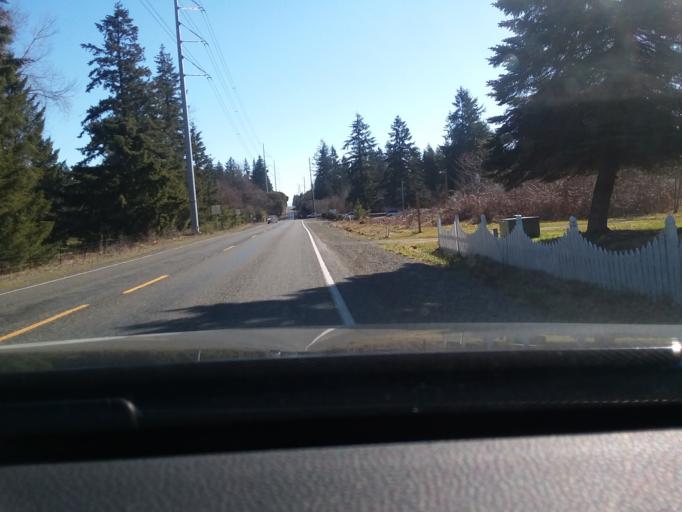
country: US
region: Washington
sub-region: Pierce County
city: Waller
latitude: 47.1807
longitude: -122.3809
